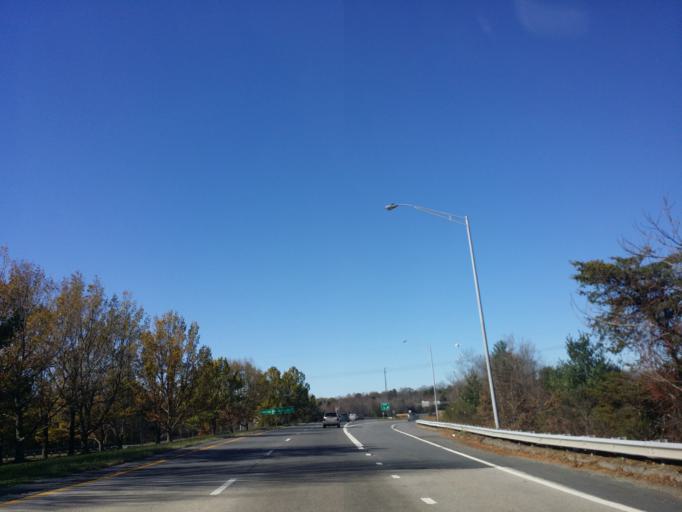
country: US
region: North Carolina
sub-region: Buncombe County
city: Biltmore Forest
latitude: 35.5672
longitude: -82.4994
